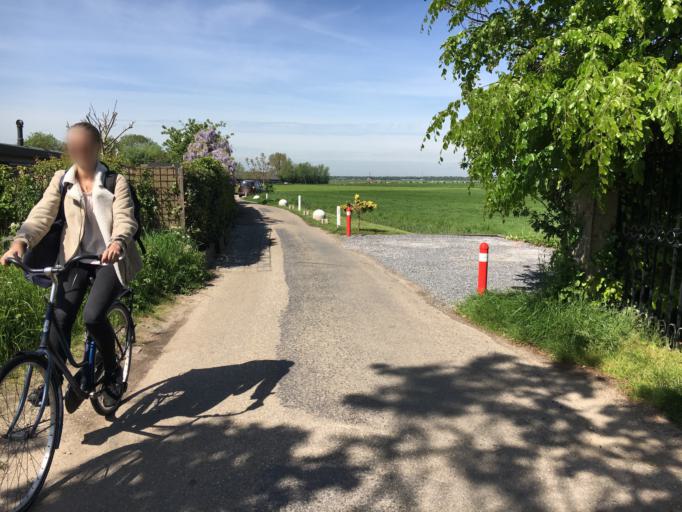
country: NL
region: North Holland
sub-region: Gemeente Weesp
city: Weesp
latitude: 52.2857
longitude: 5.0611
